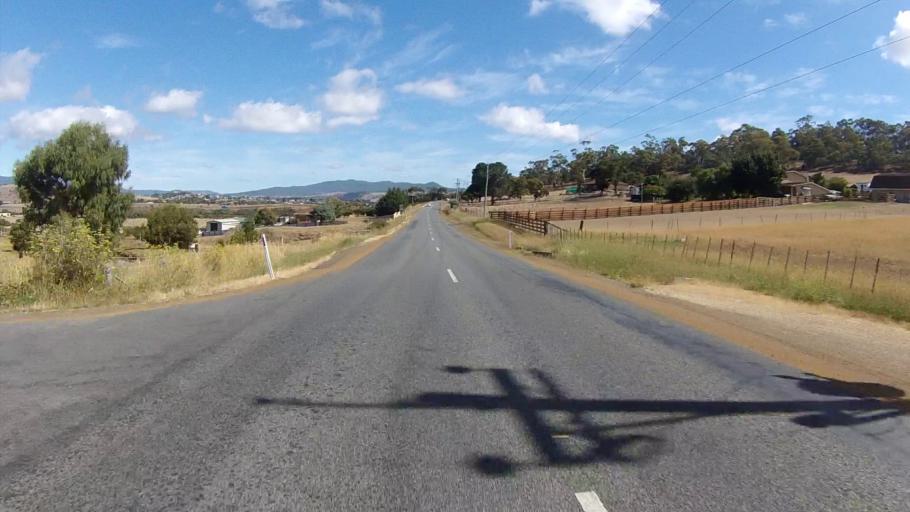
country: AU
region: Tasmania
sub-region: Brighton
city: Bridgewater
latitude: -42.7123
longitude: 147.2717
